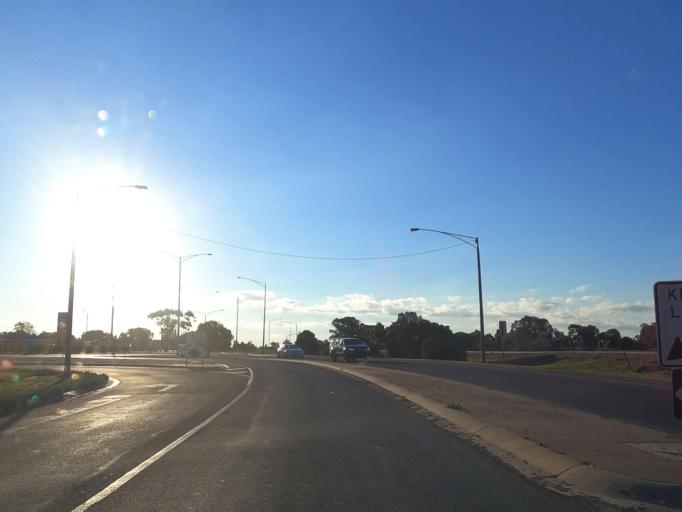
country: AU
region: Victoria
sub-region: Swan Hill
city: Swan Hill
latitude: -35.3278
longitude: 143.5541
